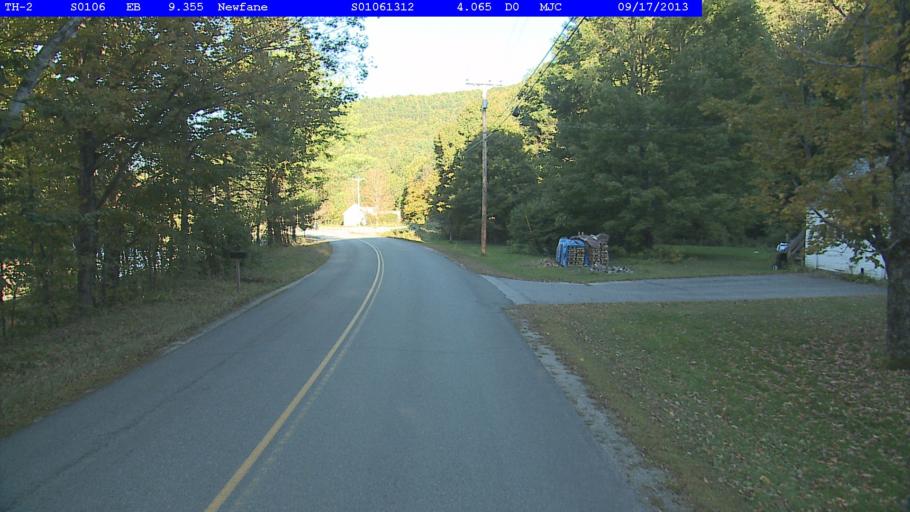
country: US
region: Vermont
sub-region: Windham County
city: Newfane
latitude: 42.9363
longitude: -72.6988
